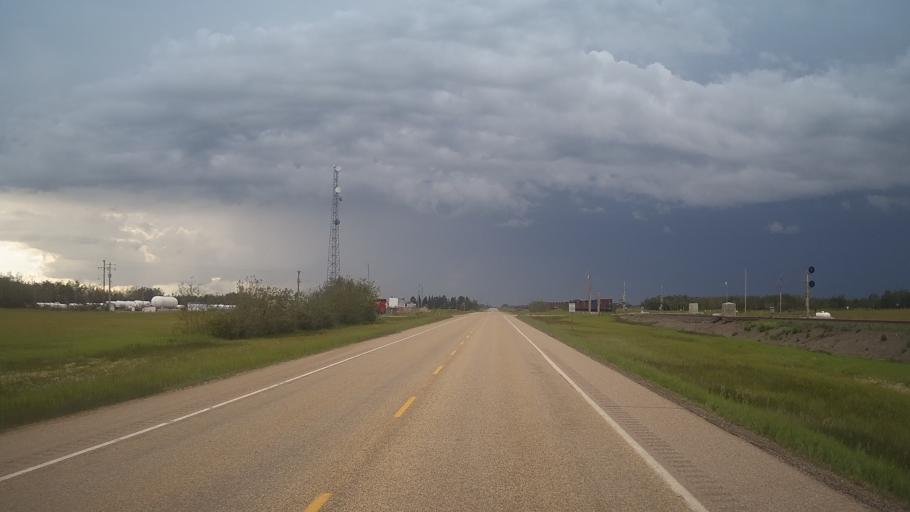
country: CA
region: Alberta
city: Tofield
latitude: 53.2684
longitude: -112.3652
